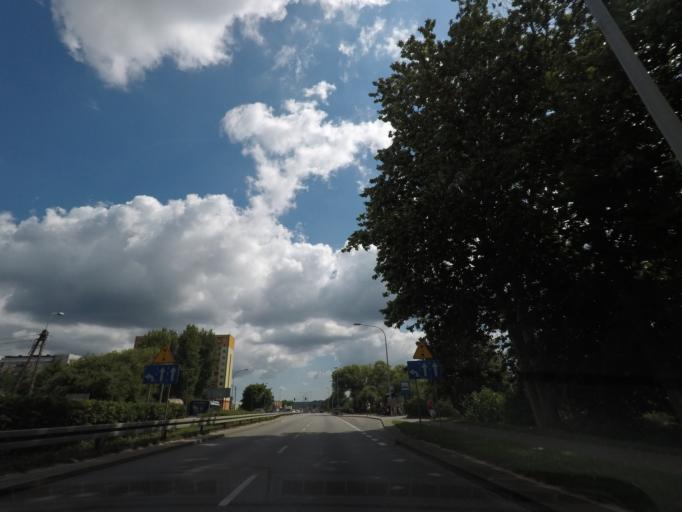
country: PL
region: Pomeranian Voivodeship
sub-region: Powiat wejherowski
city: Wejherowo
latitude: 54.6044
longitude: 18.2450
